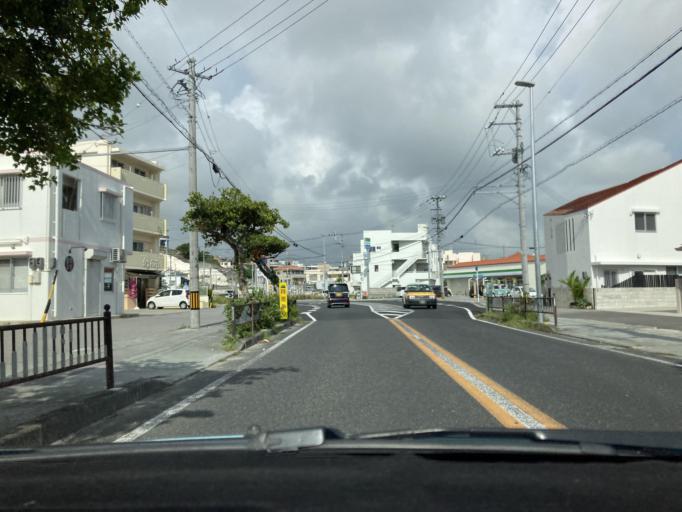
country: JP
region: Okinawa
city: Itoman
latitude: 26.1283
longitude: 127.6691
